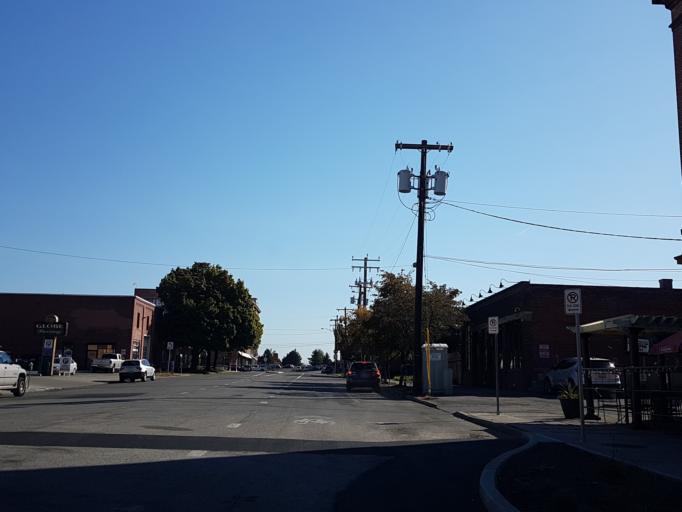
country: US
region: Washington
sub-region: Spokane County
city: Spokane
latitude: 47.6590
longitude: -117.4111
